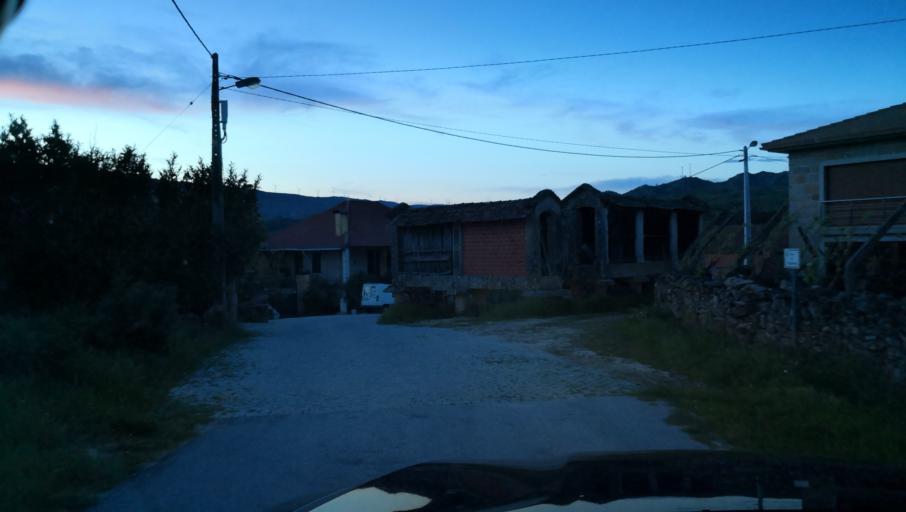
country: PT
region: Vila Real
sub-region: Vila Real
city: Vila Real
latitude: 41.3541
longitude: -7.6895
